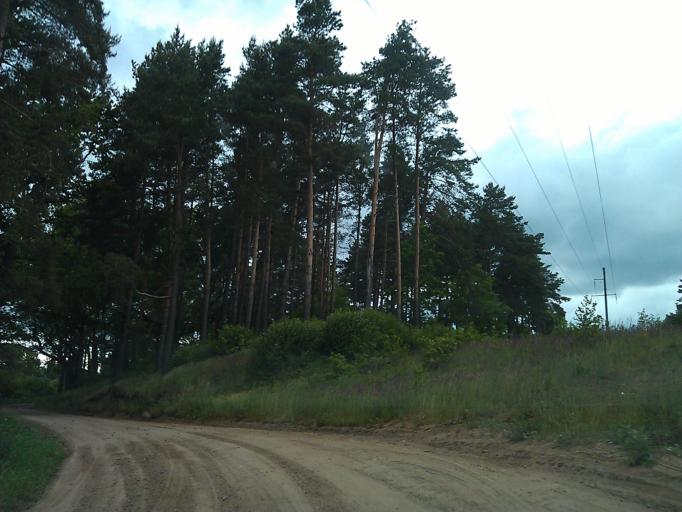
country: LV
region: Adazi
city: Adazi
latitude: 57.0830
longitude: 24.3056
